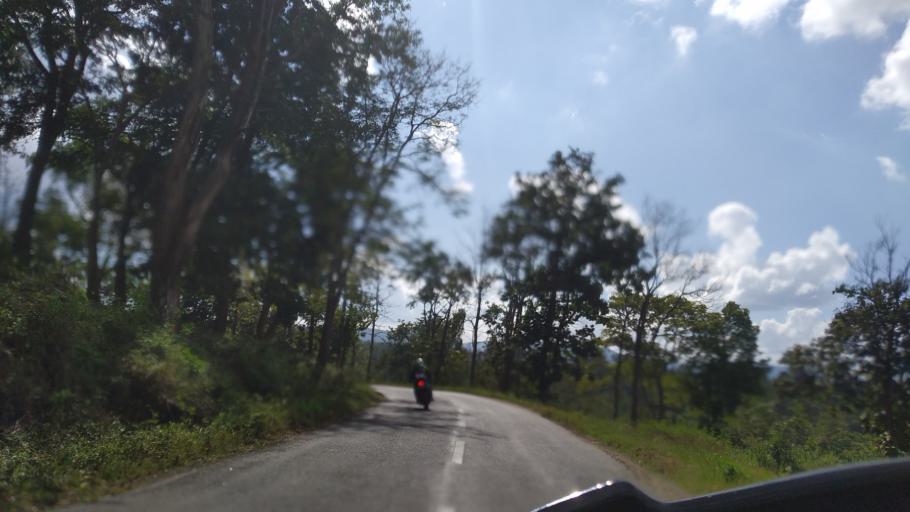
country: IN
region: Kerala
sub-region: Wayanad
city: Panamaram
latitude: 11.9169
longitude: 76.0639
